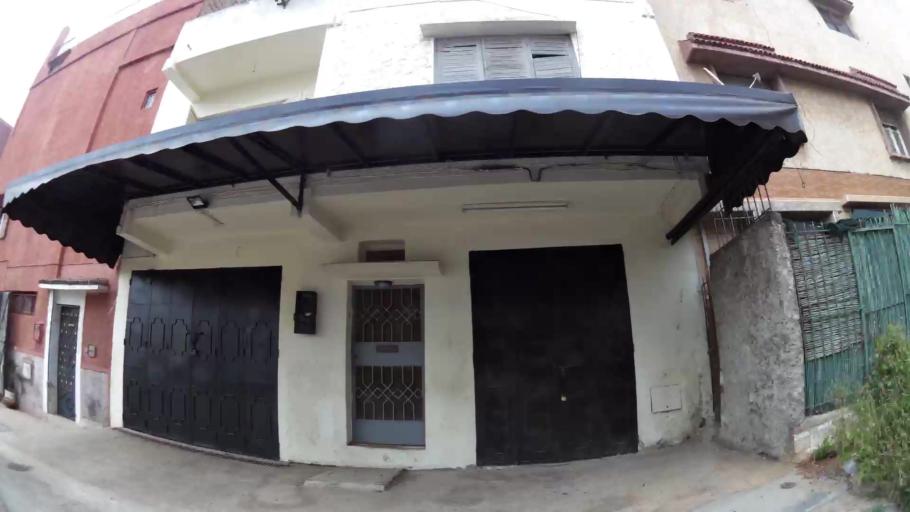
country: MA
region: Rabat-Sale-Zemmour-Zaer
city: Sale
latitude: 34.0474
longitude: -6.7954
